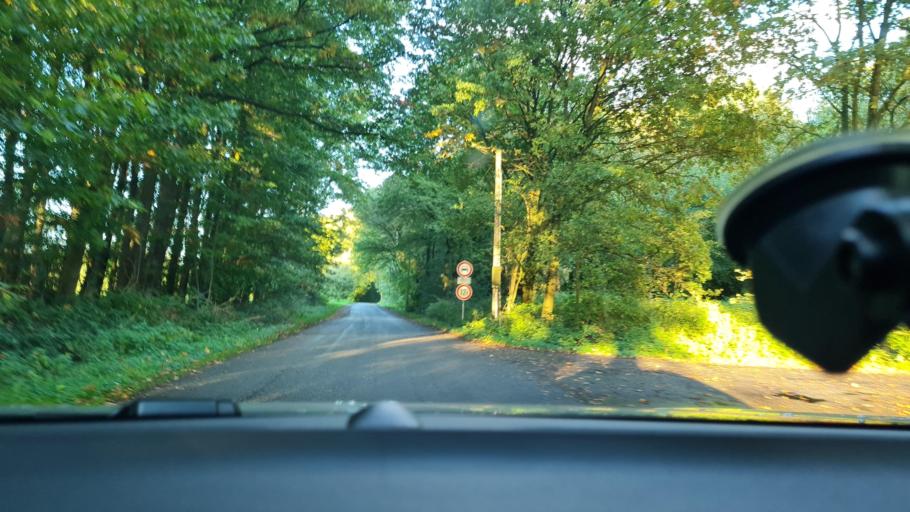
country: DE
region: North Rhine-Westphalia
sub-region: Regierungsbezirk Dusseldorf
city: Hunxe
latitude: 51.6043
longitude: 6.7709
